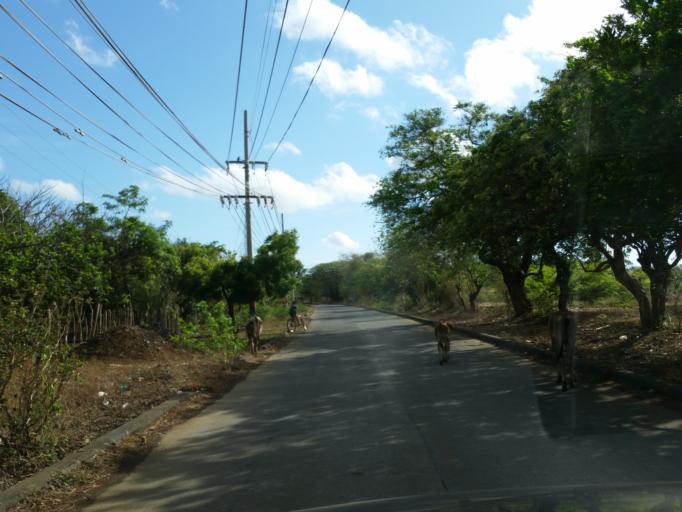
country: NI
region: Masaya
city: Masaya
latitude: 12.0044
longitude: -86.0847
